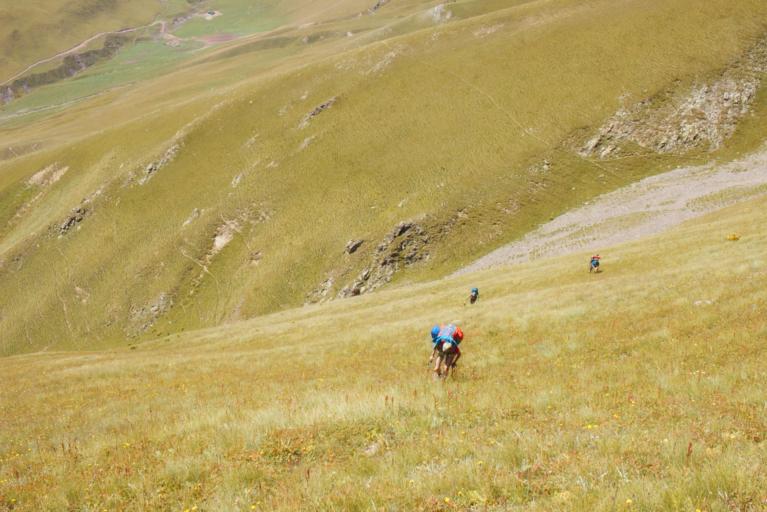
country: RU
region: Karachayevo-Cherkesiya
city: Mednogorskiy
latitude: 43.6137
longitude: 41.0930
